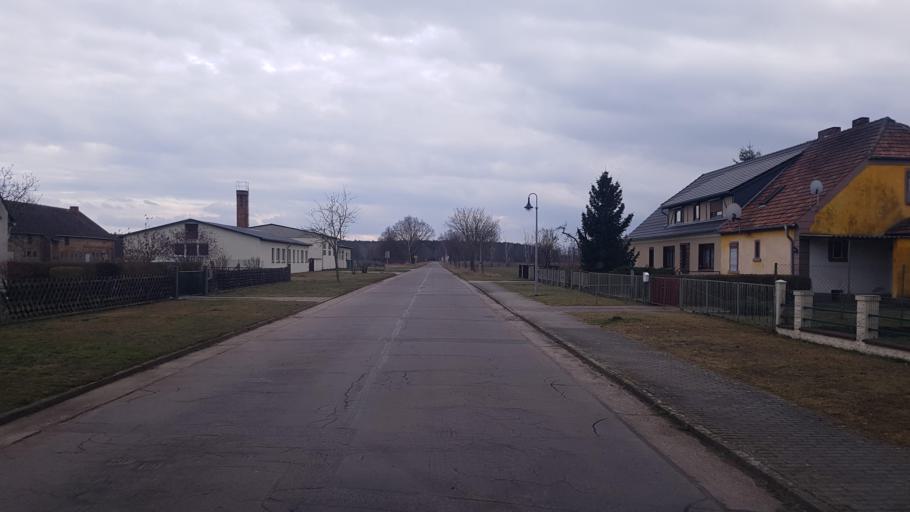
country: DE
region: Brandenburg
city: Drahnsdorf
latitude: 51.9218
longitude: 13.6414
